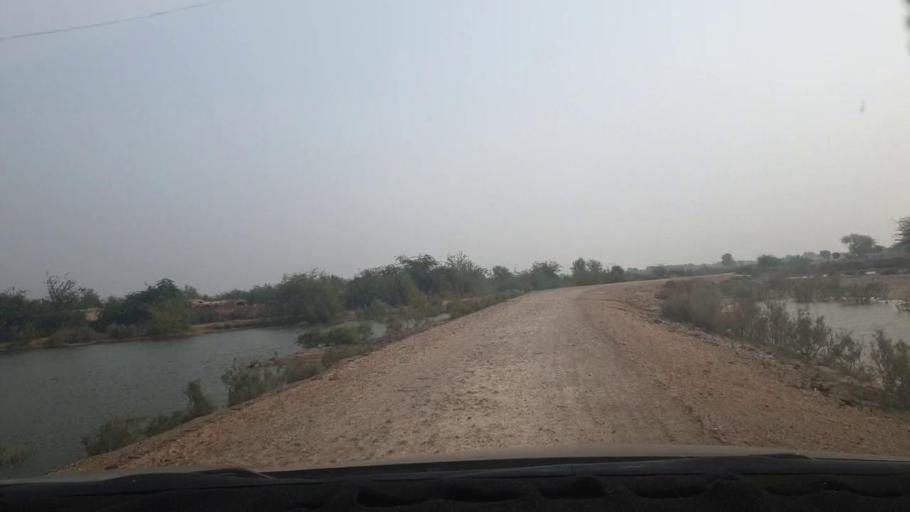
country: PK
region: Sindh
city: Jamshoro
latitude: 25.5227
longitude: 68.3142
